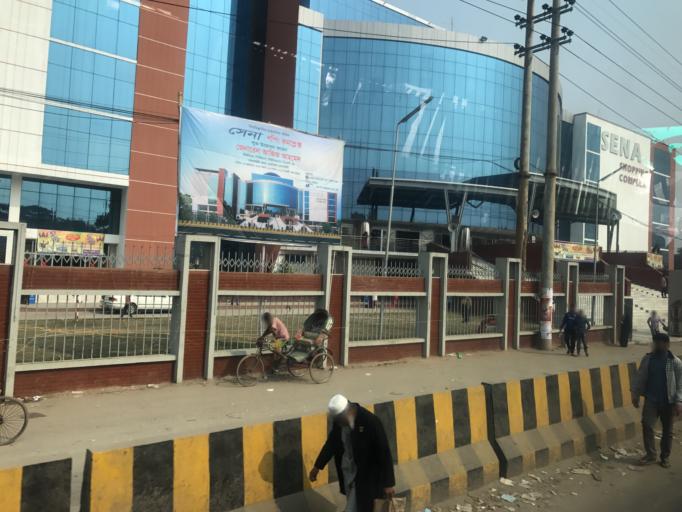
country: BD
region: Dhaka
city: Tungi
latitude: 23.9127
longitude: 90.2595
